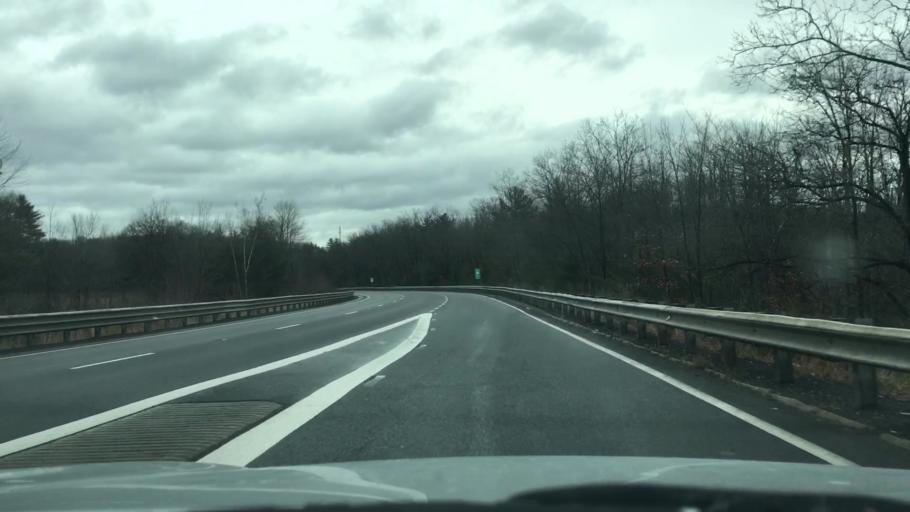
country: US
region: Massachusetts
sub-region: Franklin County
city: Turners Falls
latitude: 42.6086
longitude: -72.5820
